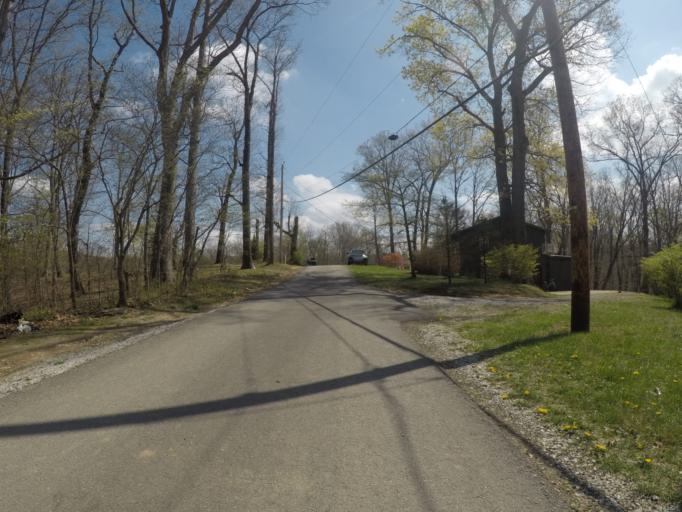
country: US
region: Ohio
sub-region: Lawrence County
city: Burlington
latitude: 38.3913
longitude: -82.5350
